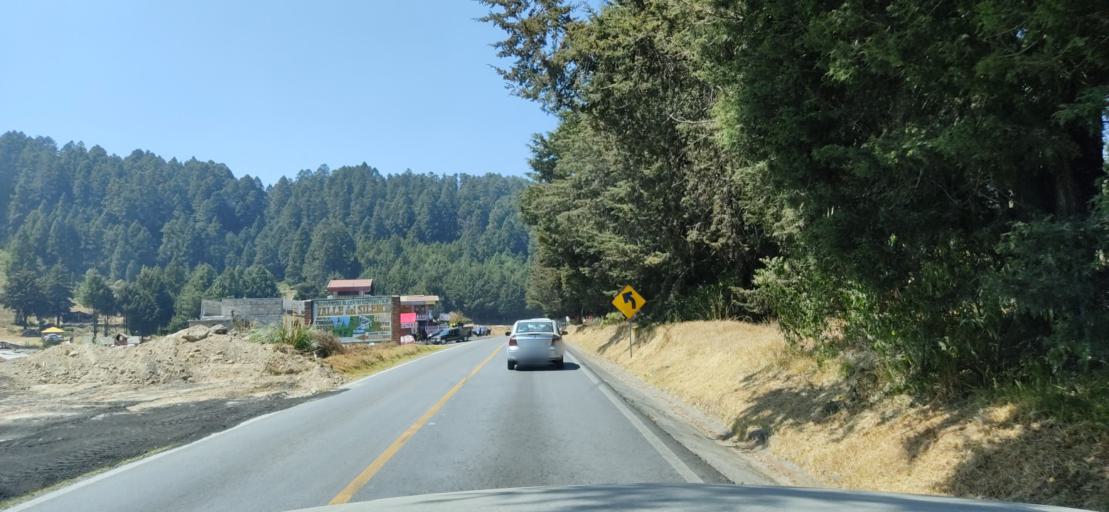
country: MX
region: Mexico
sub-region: Ocoyoacac
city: San Jeronimo Acazulco
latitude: 19.2807
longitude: -99.3788
